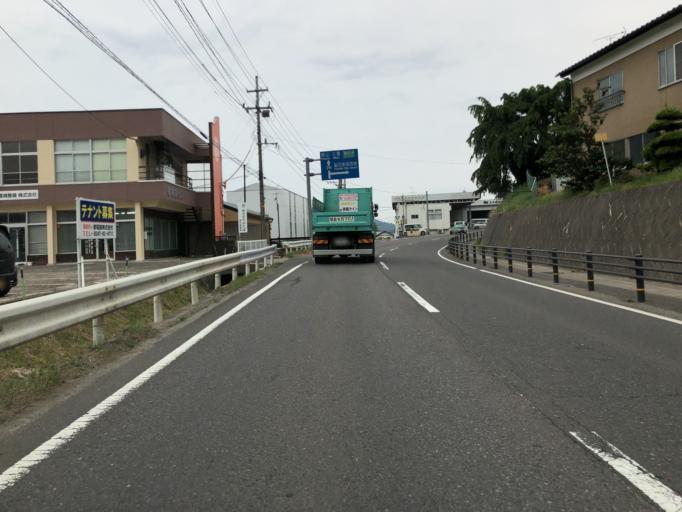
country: JP
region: Fukushima
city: Funehikimachi-funehiki
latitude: 37.4346
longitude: 140.5879
